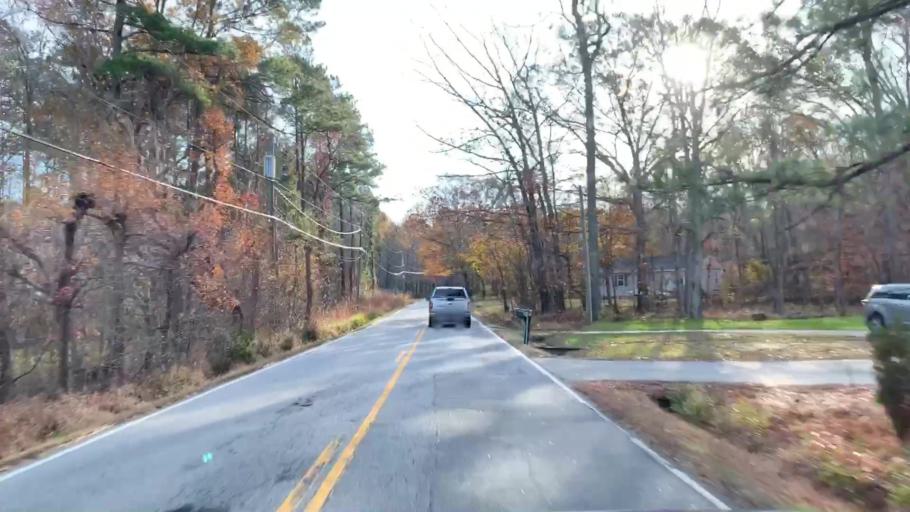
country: US
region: Virginia
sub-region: City of Virginia Beach
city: Virginia Beach
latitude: 36.7371
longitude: -76.1025
